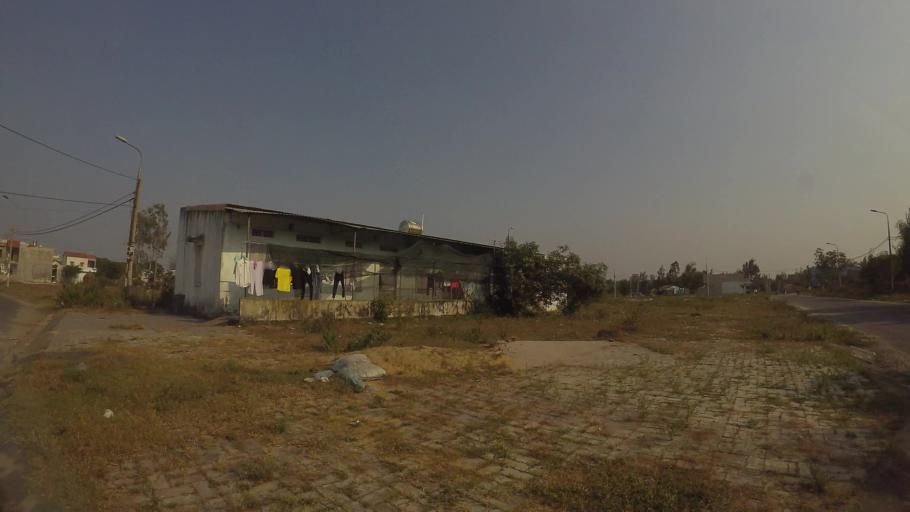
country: VN
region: Da Nang
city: Ngu Hanh Son
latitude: 15.9529
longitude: 108.2562
